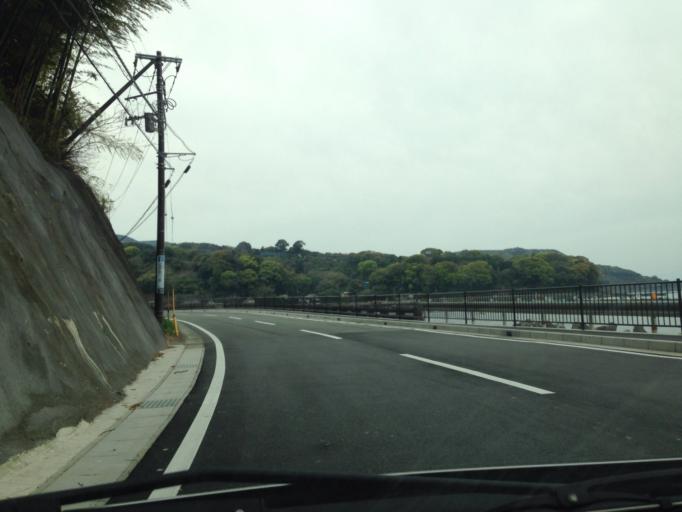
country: JP
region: Shizuoka
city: Heda
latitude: 35.0170
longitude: 138.8495
